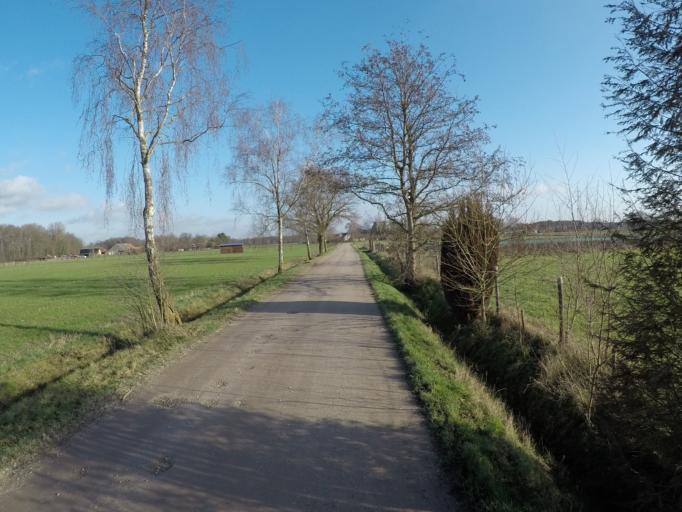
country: BE
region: Flanders
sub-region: Provincie Antwerpen
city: Zandhoven
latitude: 51.2251
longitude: 4.6549
